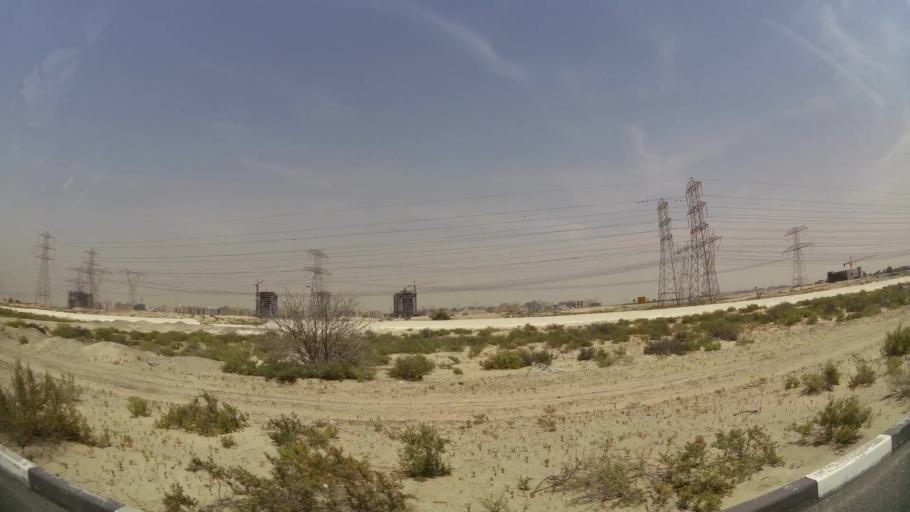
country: AE
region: Ash Shariqah
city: Sharjah
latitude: 25.1898
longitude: 55.3876
